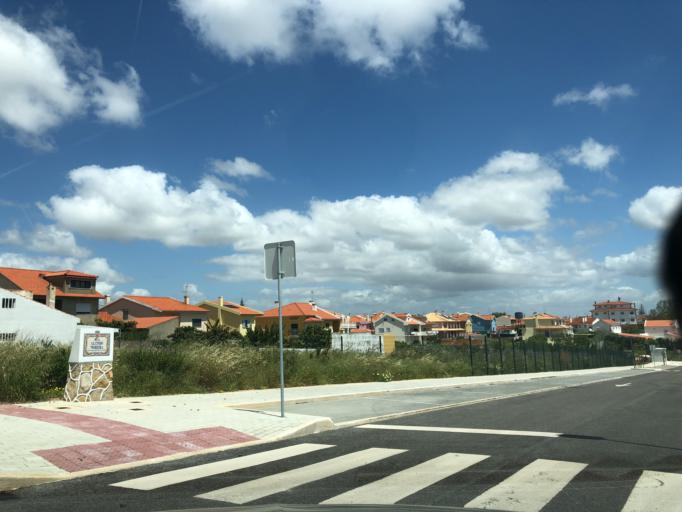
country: PT
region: Lisbon
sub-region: Cascais
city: Sao Domingos de Rana
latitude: 38.7055
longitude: -9.3289
